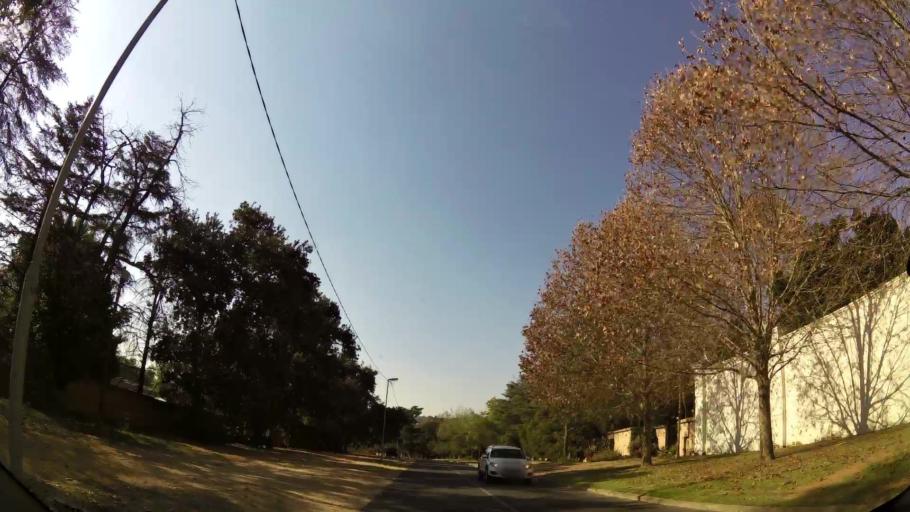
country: ZA
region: Gauteng
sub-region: City of Johannesburg Metropolitan Municipality
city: Diepsloot
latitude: -26.0632
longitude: 28.0119
